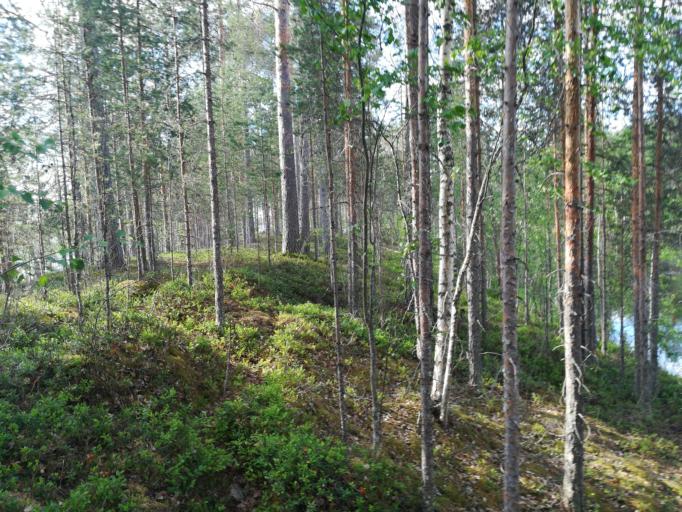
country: FI
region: Southern Savonia
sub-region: Savonlinna
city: Savonlinna
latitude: 61.6418
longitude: 28.7131
